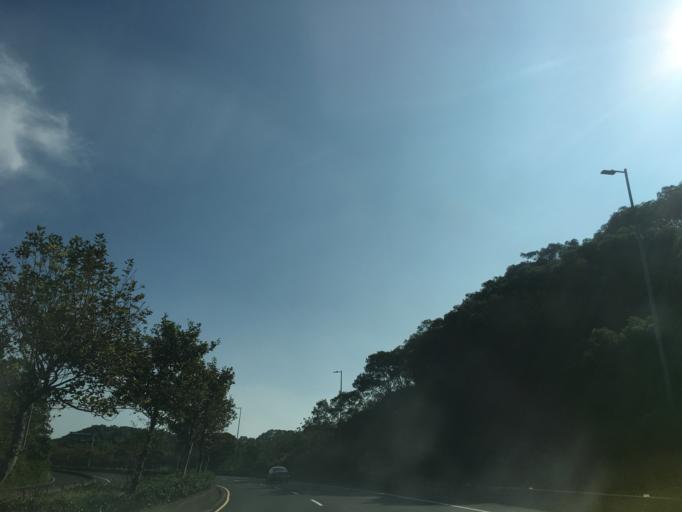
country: TW
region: Taiwan
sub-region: Hsinchu
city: Hsinchu
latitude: 24.7704
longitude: 120.9521
